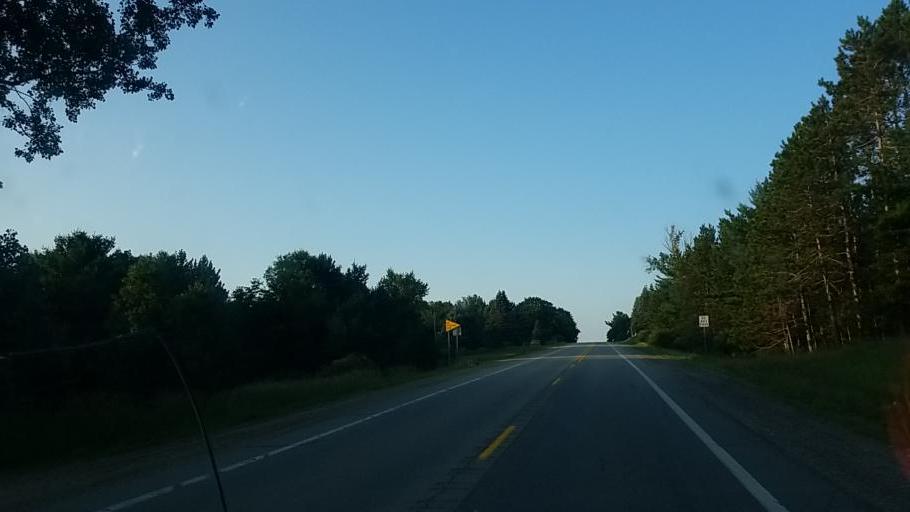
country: US
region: Michigan
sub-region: Isabella County
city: Lake Isabella
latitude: 43.6806
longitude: -85.1465
